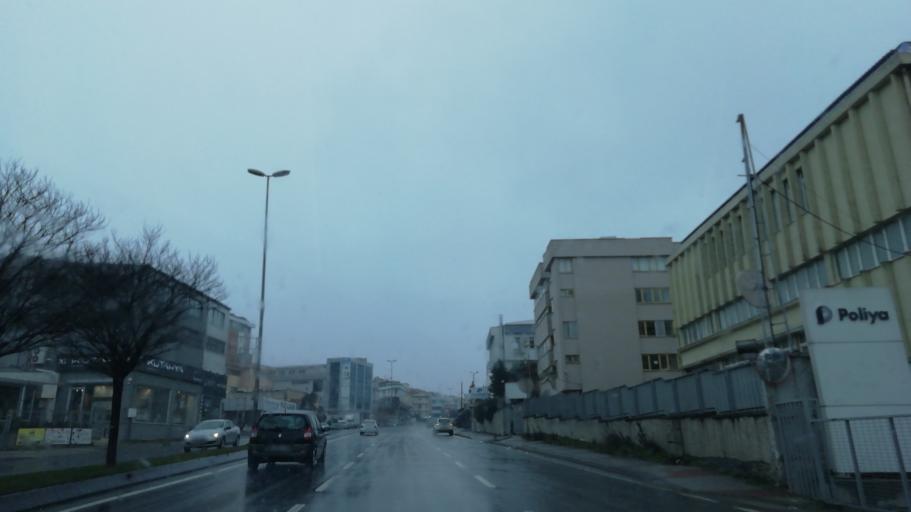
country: TR
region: Istanbul
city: Yakuplu
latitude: 40.9960
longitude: 28.7149
